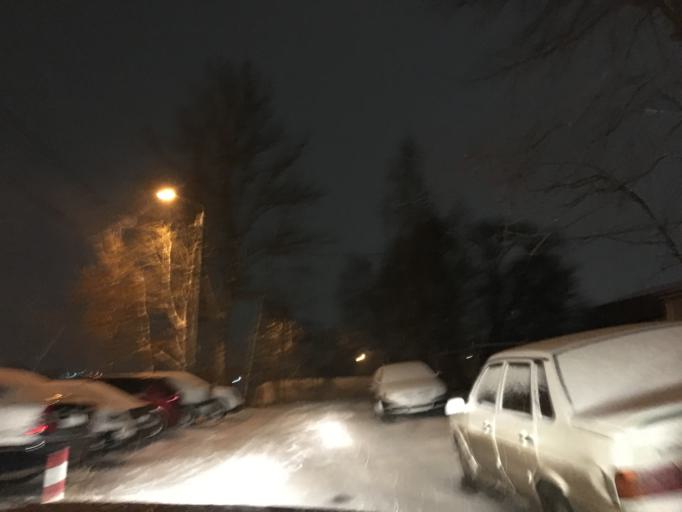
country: RU
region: Tula
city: Mendeleyevskiy
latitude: 54.1674
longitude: 37.5626
